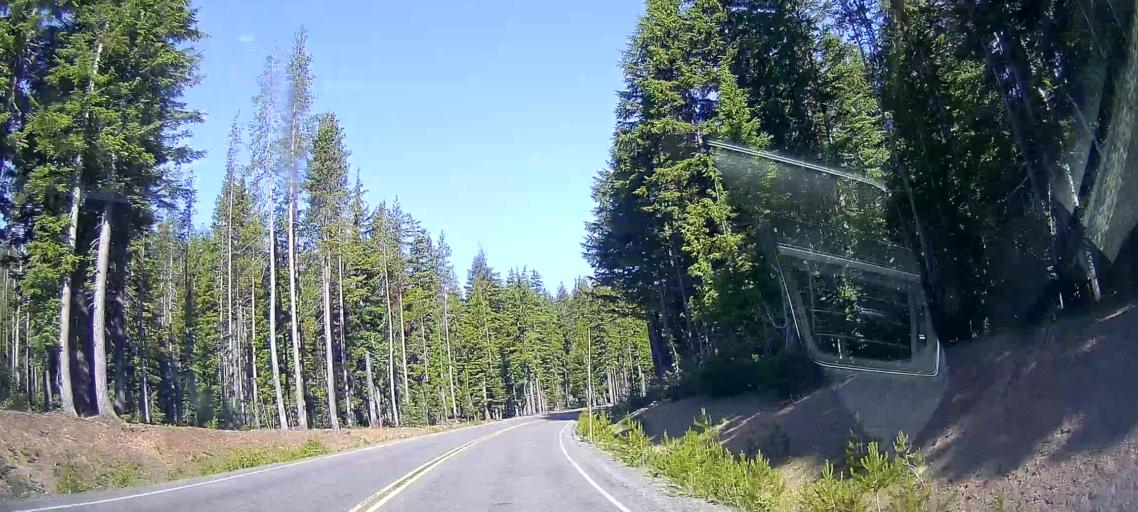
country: US
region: Oregon
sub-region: Jackson County
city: Shady Cove
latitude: 42.8604
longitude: -122.1636
